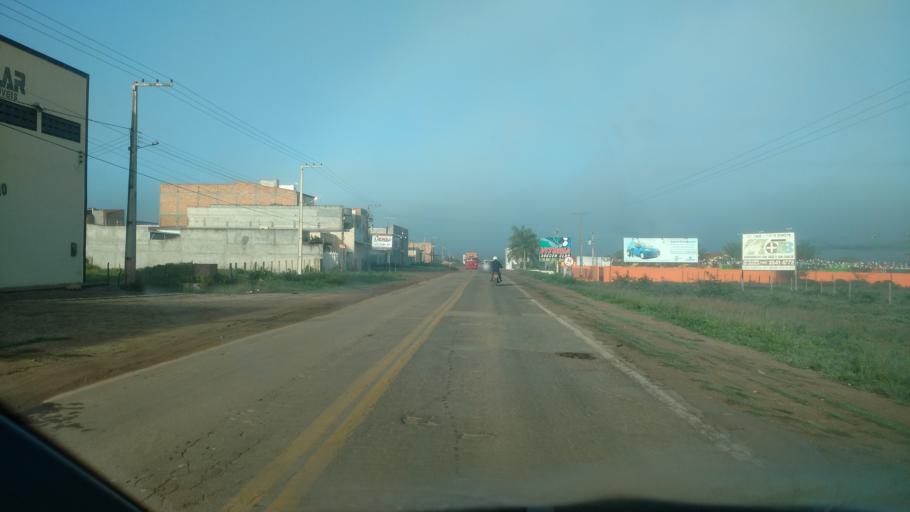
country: BR
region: Sergipe
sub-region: Tobias Barreto
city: Tobias Barreto
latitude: -11.1729
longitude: -37.9880
